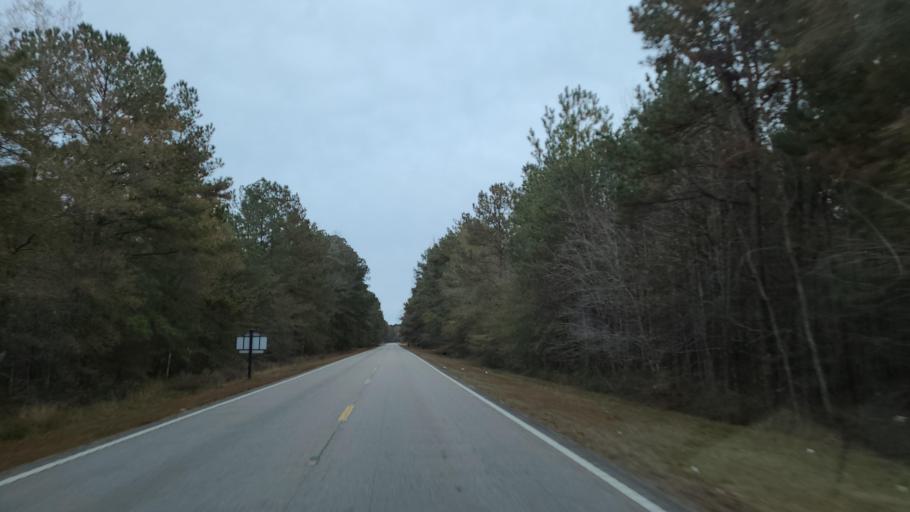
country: US
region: Mississippi
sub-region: Clarke County
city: Stonewall
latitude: 32.0328
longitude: -88.8701
